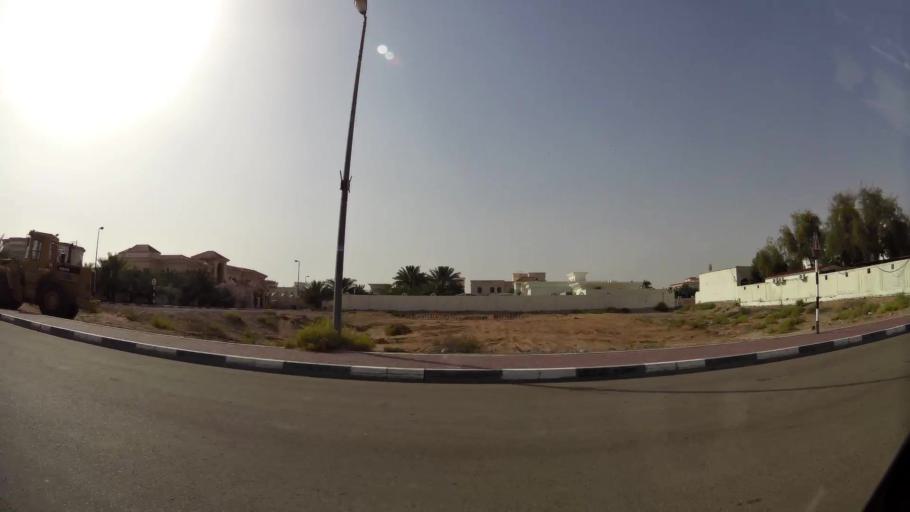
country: AE
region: Abu Dhabi
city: Al Ain
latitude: 24.2255
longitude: 55.6572
